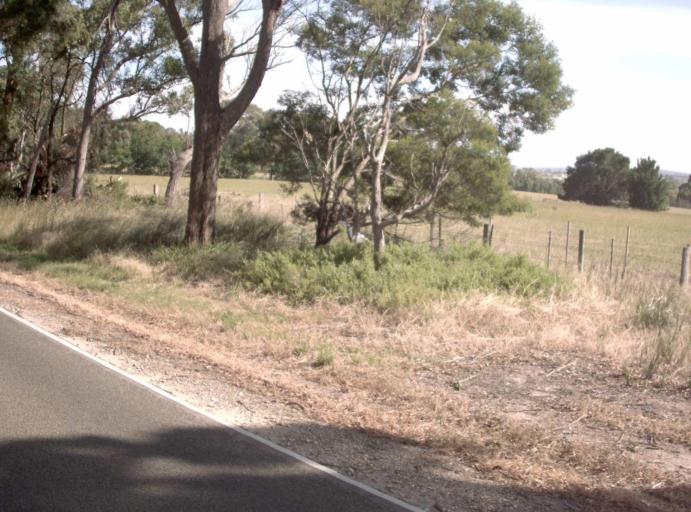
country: AU
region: Victoria
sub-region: East Gippsland
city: Lakes Entrance
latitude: -37.8093
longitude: 147.8438
